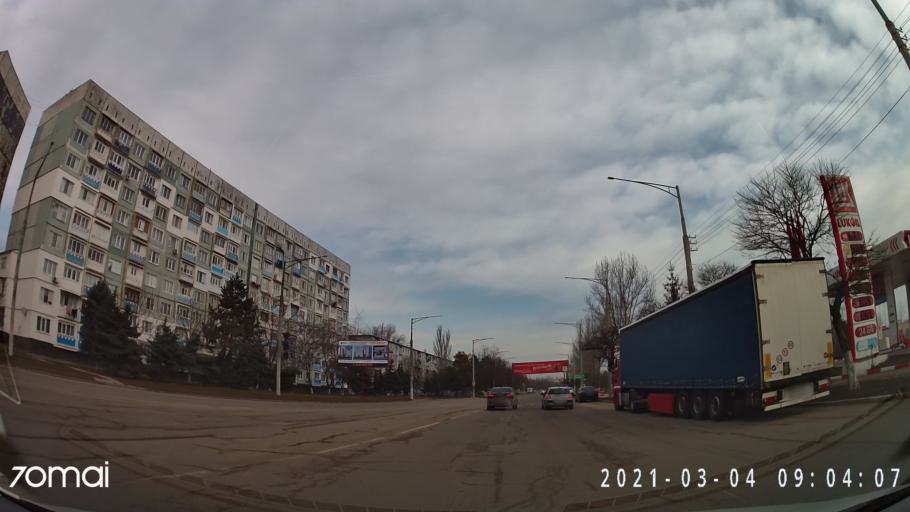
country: MD
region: Balti
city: Balti
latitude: 47.7559
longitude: 27.9415
